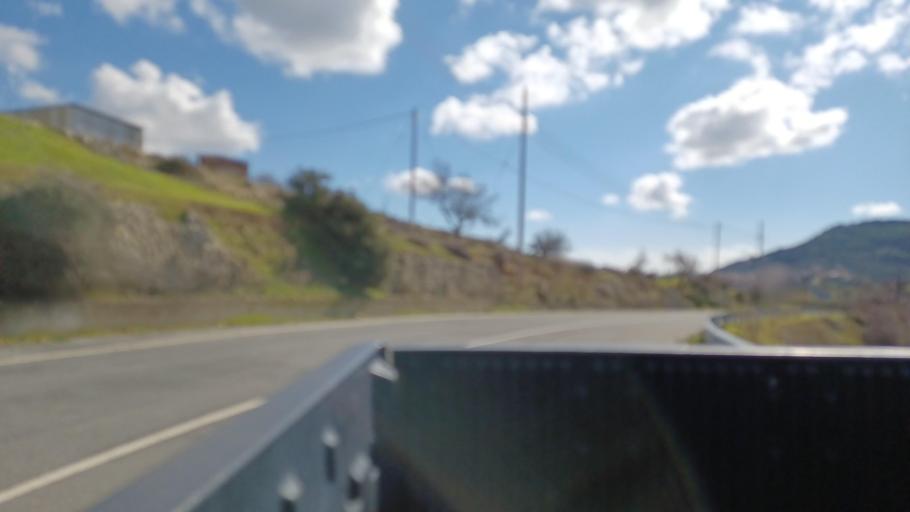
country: CY
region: Limassol
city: Pachna
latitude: 34.7905
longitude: 32.7373
